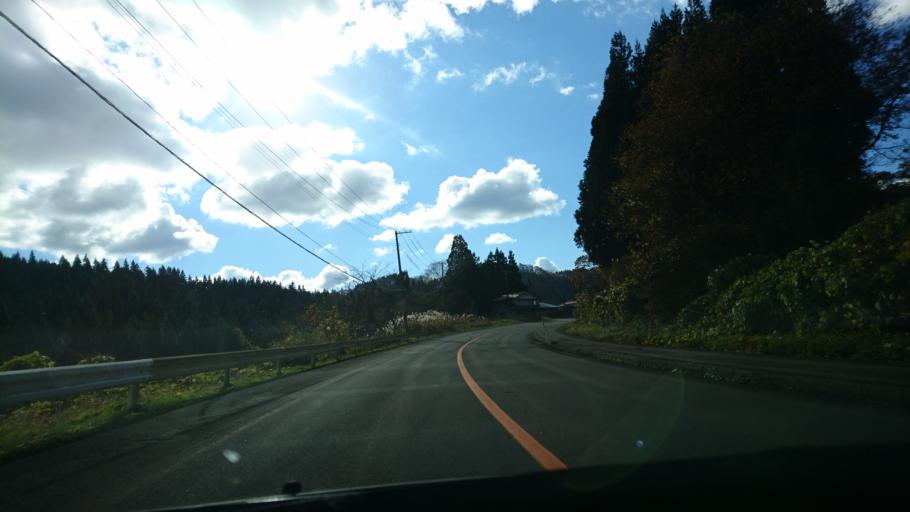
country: JP
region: Akita
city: Omagari
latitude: 39.3074
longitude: 140.2543
